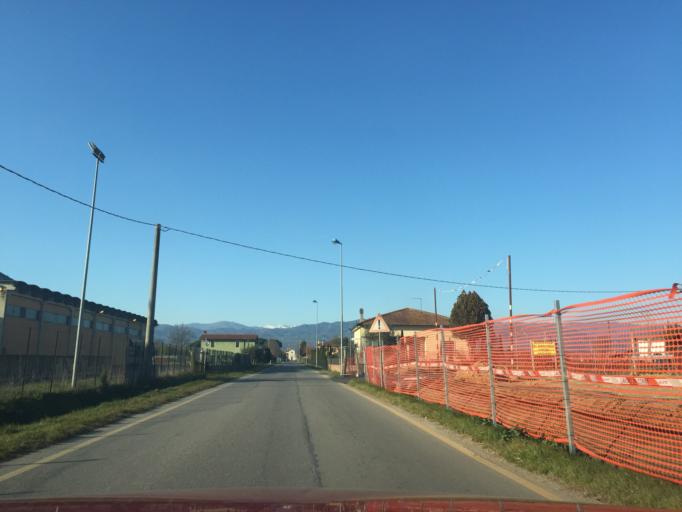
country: IT
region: Tuscany
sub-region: Provincia di Pistoia
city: Ponte Buggianese
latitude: 43.8408
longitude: 10.7615
